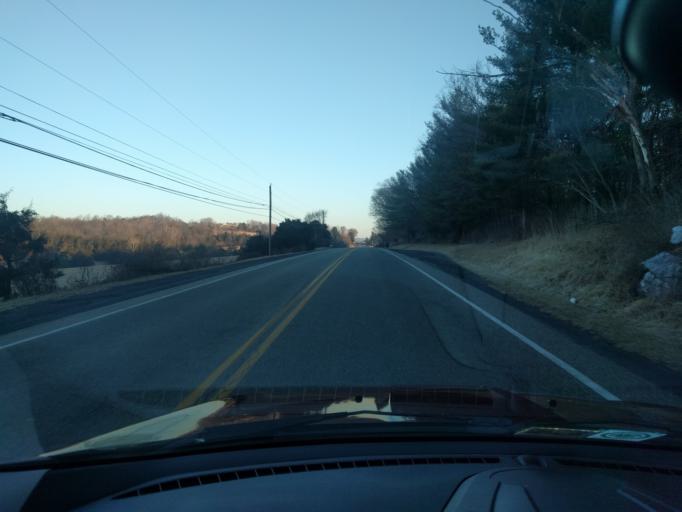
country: US
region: Virginia
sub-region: Augusta County
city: Weyers Cave
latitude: 38.3139
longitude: -78.9360
